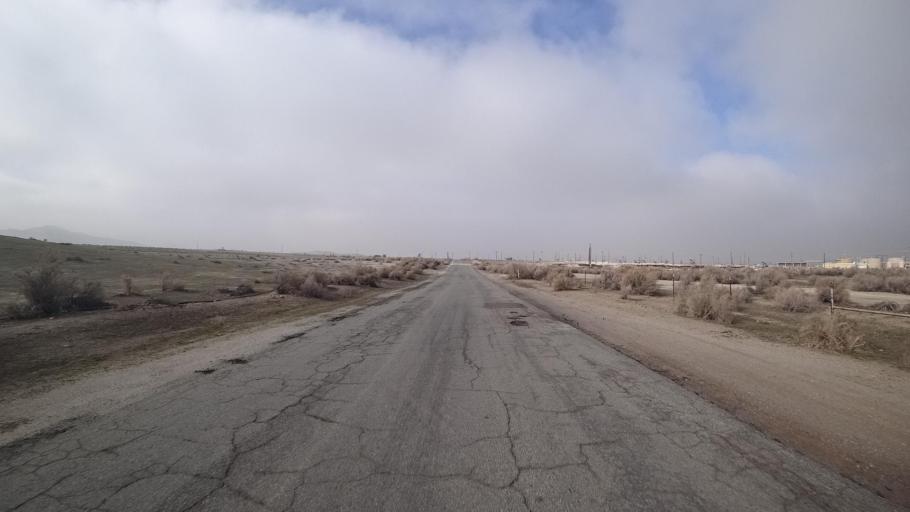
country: US
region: California
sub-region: Kern County
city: Maricopa
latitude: 35.0299
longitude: -119.3433
